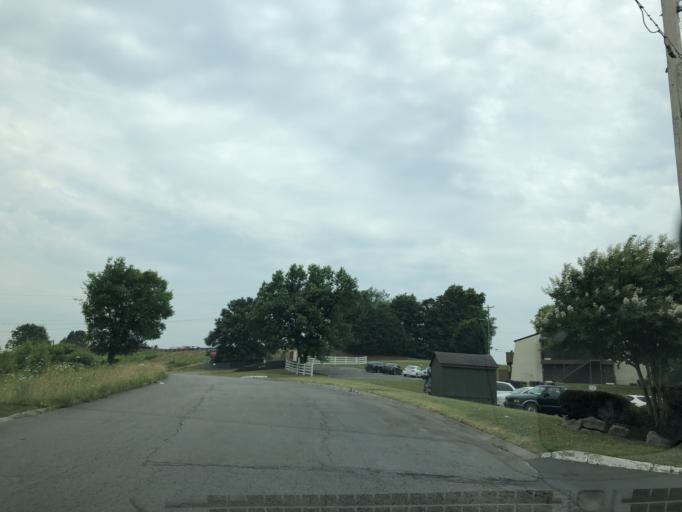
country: US
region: Tennessee
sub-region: Davidson County
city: Oak Hill
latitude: 36.0716
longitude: -86.6857
